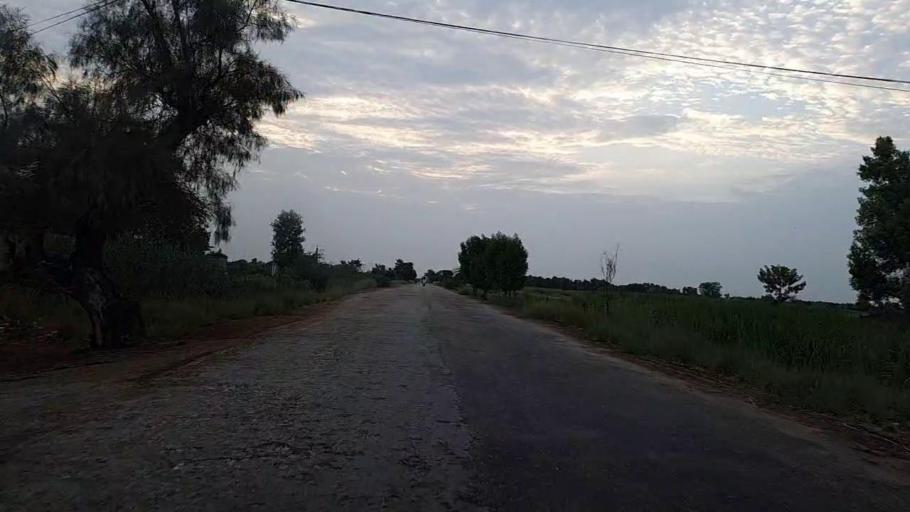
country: PK
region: Sindh
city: Naushahro Firoz
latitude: 26.8198
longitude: 68.1708
